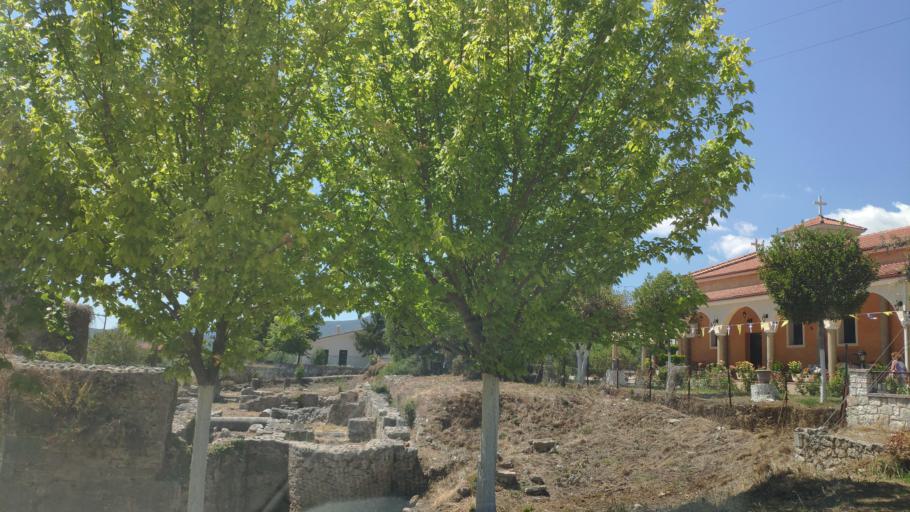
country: GR
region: Epirus
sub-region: Nomos Prevezis
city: Kanalaki
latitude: 39.3265
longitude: 20.6071
